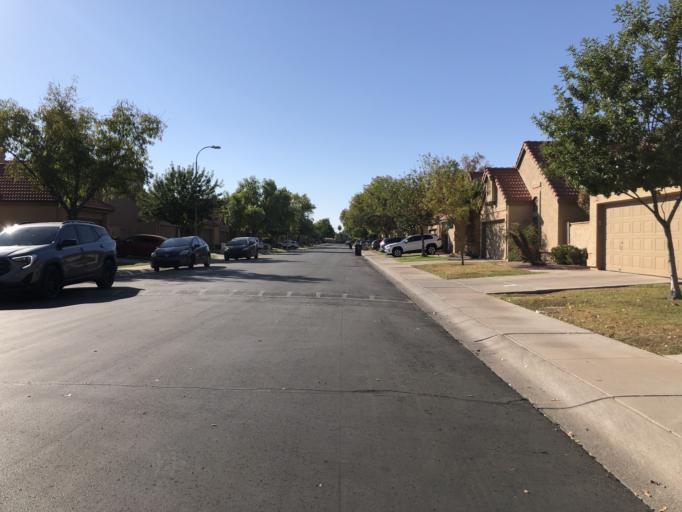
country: US
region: Arizona
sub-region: Maricopa County
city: Guadalupe
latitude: 33.3168
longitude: -111.9207
